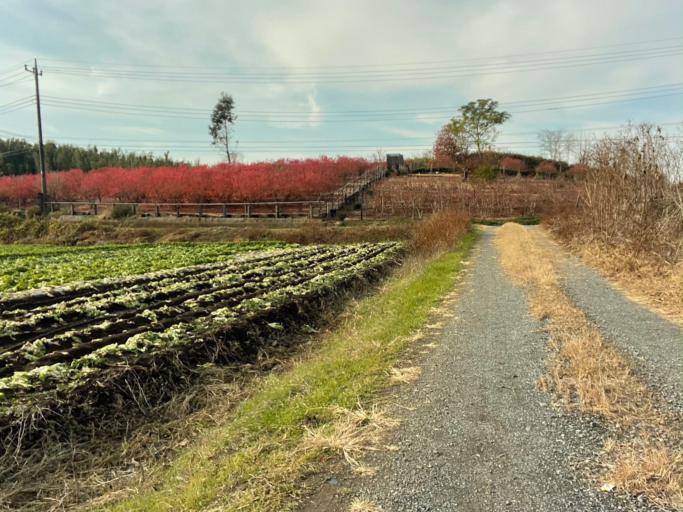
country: JP
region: Saitama
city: Kodamacho-kodamaminami
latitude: 36.1657
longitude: 139.1729
